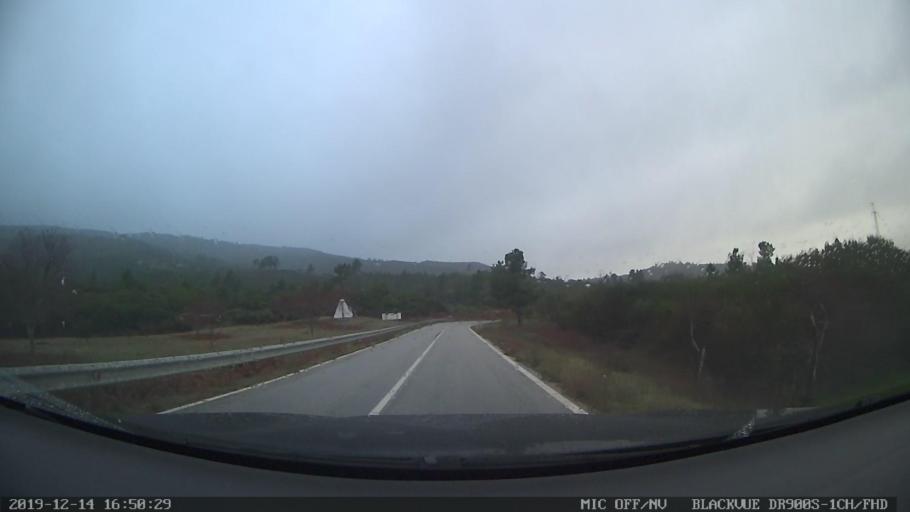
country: PT
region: Vila Real
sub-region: Murca
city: Murca
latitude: 41.4166
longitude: -7.5051
